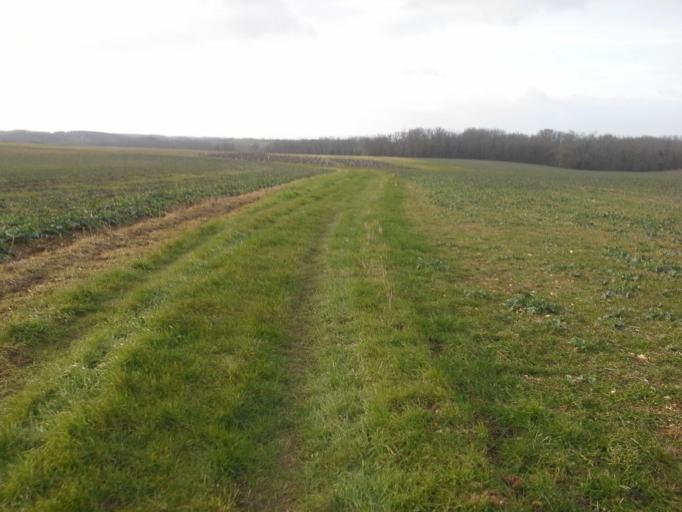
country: FR
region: Centre
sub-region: Departement du Loir-et-Cher
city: Villiers-sur-Loir
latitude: 47.8136
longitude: 0.9716
